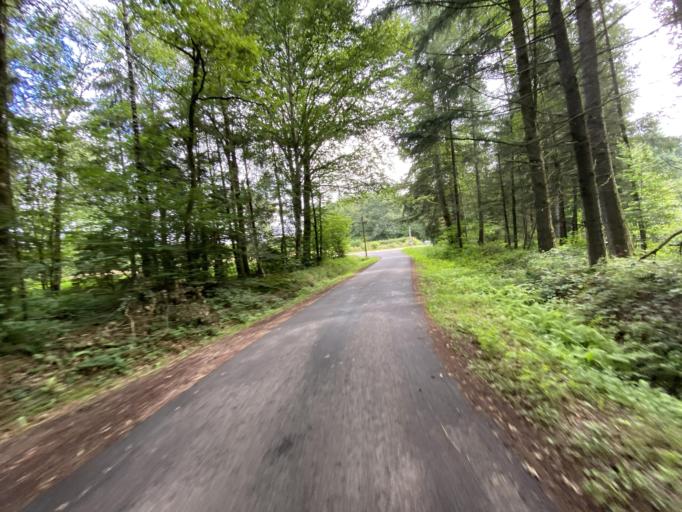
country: FR
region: Bourgogne
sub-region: Departement de la Cote-d'Or
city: Saulieu
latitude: 47.2885
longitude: 4.1701
